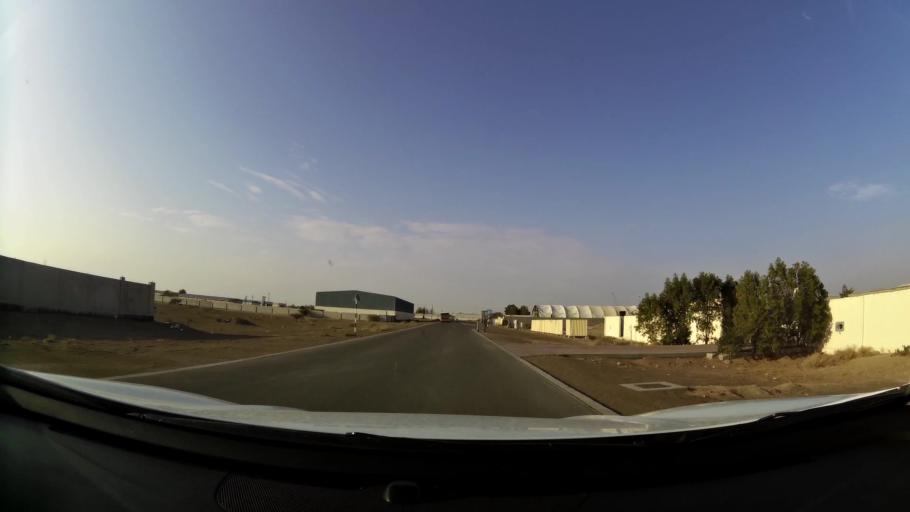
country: AE
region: Abu Dhabi
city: Al Ain
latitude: 24.1379
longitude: 55.8219
